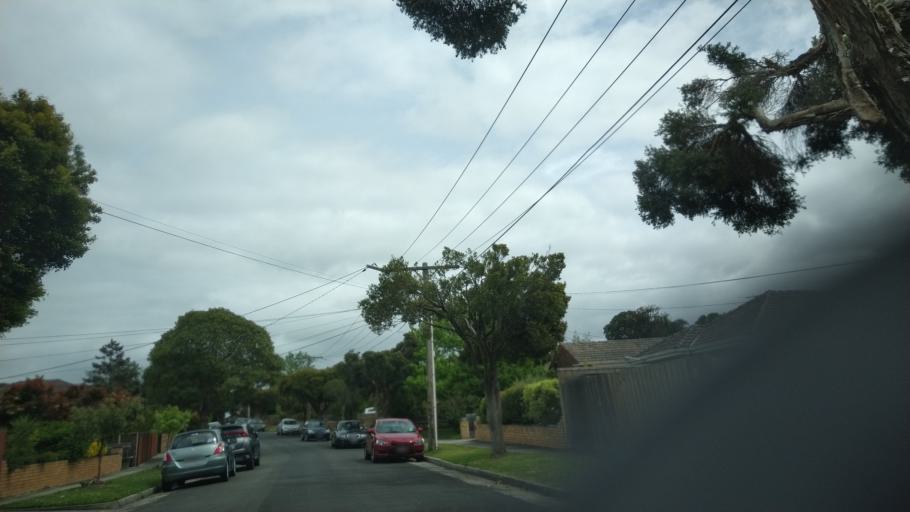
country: AU
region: Victoria
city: Murrumbeena
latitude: -37.8965
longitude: 145.0674
